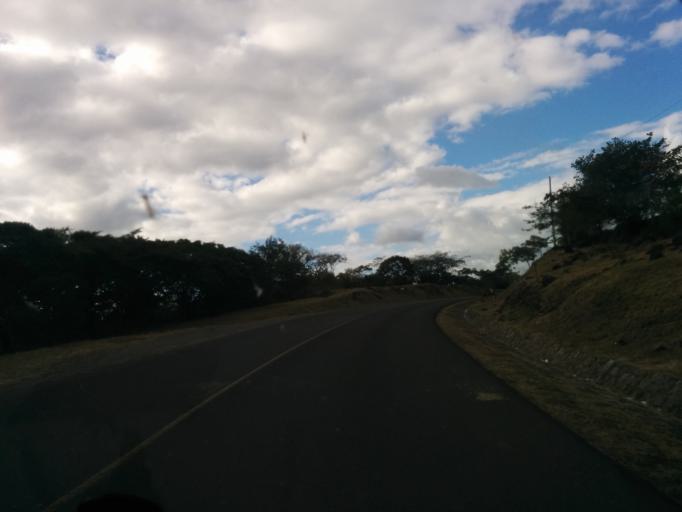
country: NI
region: Esteli
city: Esteli
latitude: 13.1876
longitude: -86.3702
